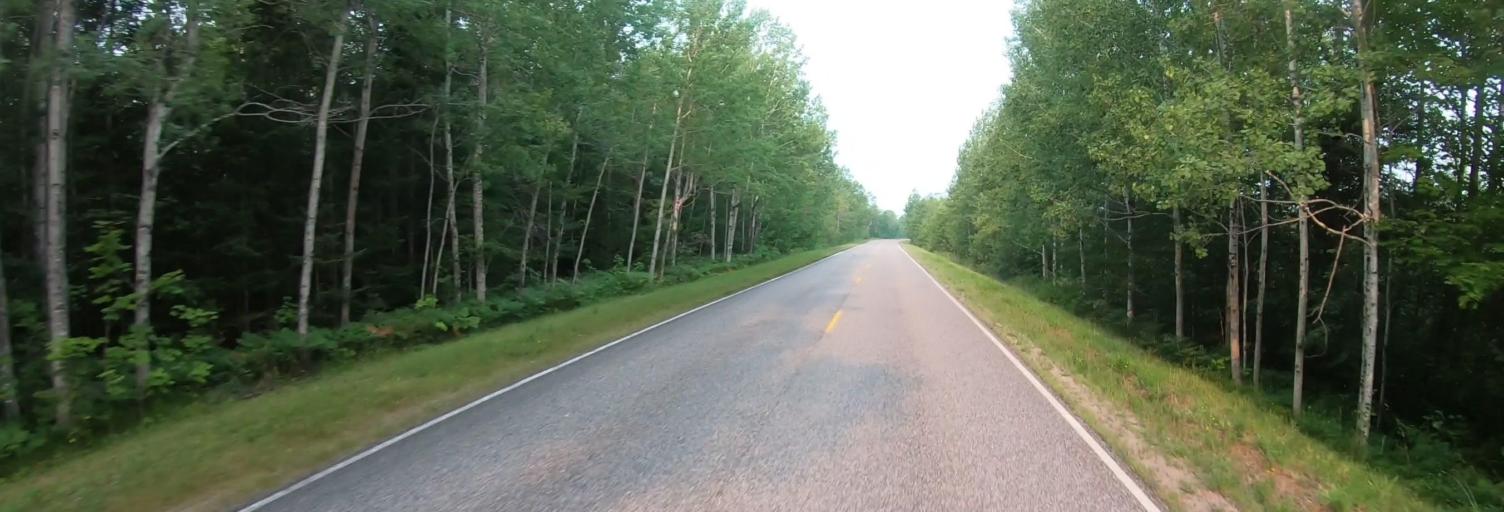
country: US
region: Michigan
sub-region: Chippewa County
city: Sault Ste. Marie
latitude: 46.4649
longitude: -84.8867
